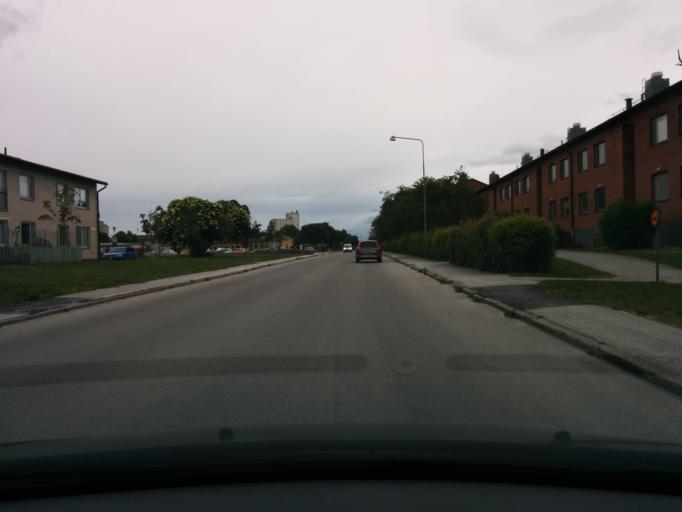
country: SE
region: Gotland
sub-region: Gotland
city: Slite
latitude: 57.7034
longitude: 18.7993
